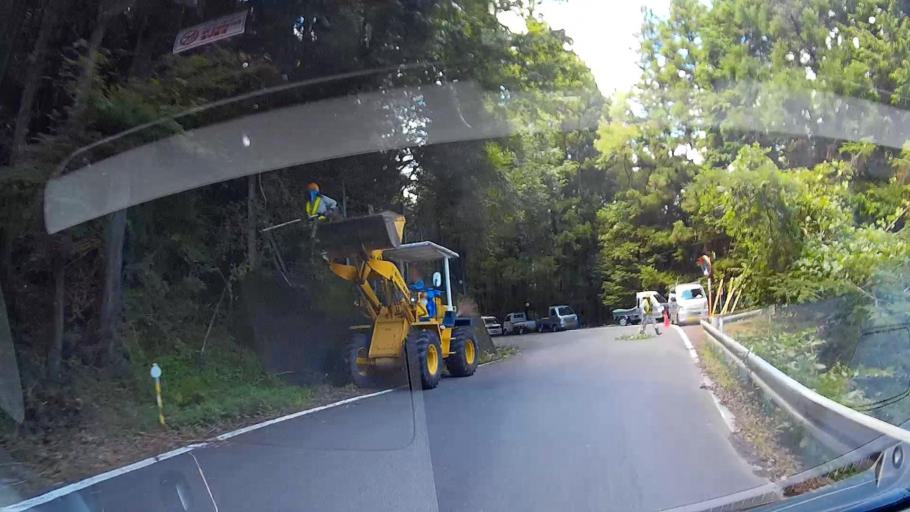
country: JP
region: Shizuoka
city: Shizuoka-shi
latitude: 35.2047
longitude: 138.2309
